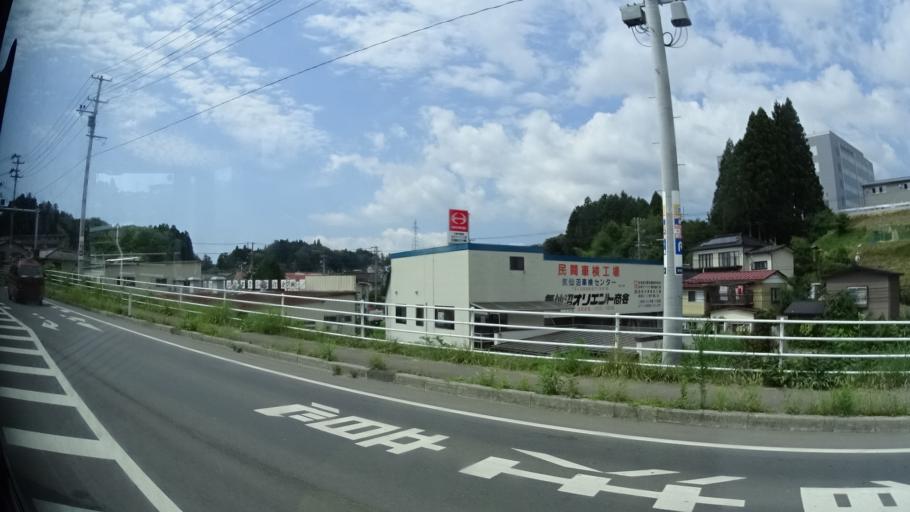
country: JP
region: Iwate
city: Ofunato
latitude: 38.8878
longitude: 141.5715
